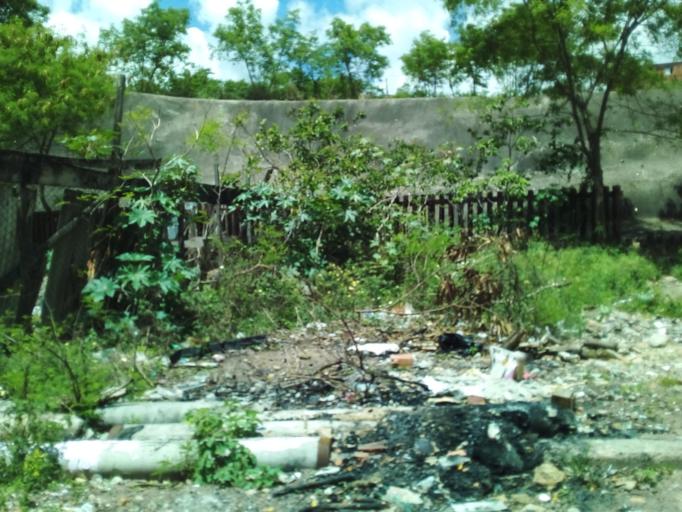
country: BR
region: Espirito Santo
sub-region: Serra
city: Serra
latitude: -20.2175
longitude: -40.2791
